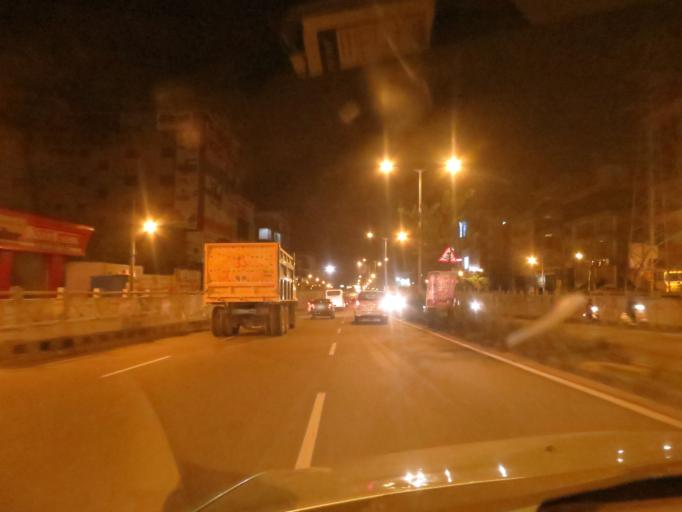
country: IN
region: Karnataka
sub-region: Bangalore Urban
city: Bangalore
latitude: 13.0177
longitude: 77.6588
